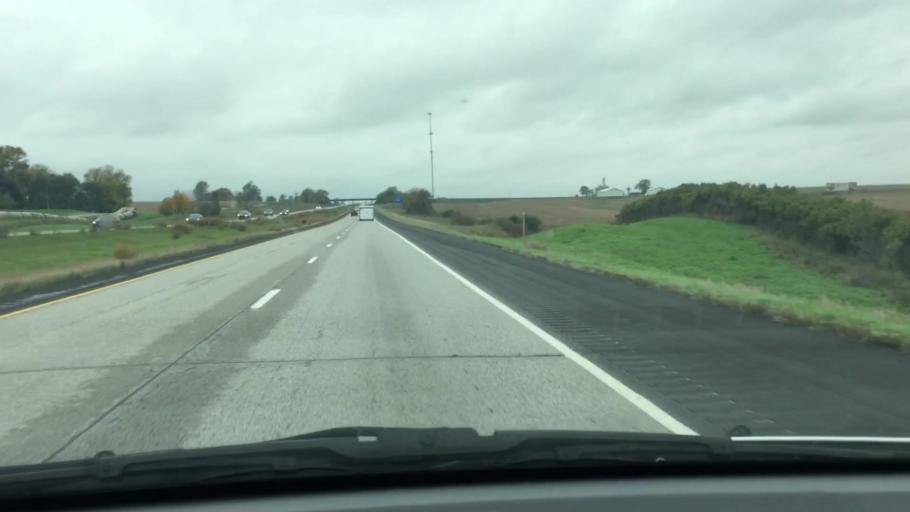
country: US
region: Iowa
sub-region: Iowa County
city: Williamsburg
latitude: 41.6873
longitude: -91.8411
